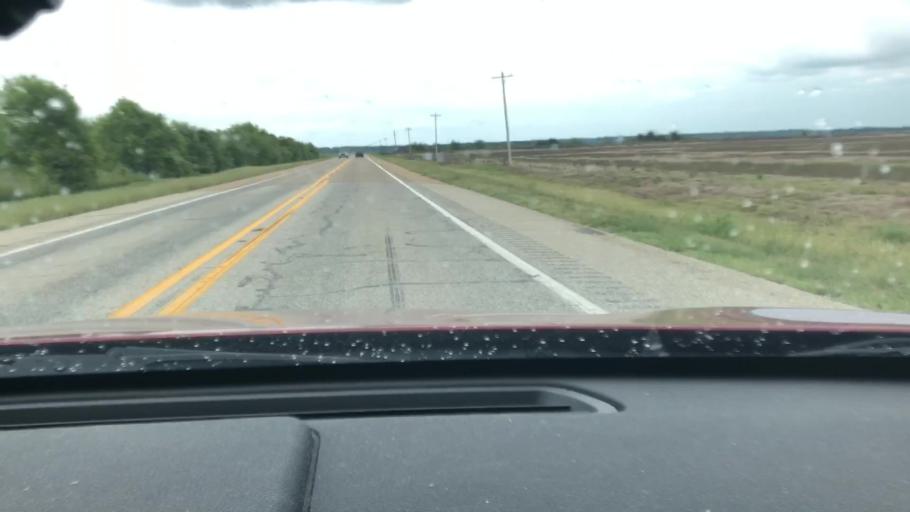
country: US
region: Arkansas
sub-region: Lafayette County
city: Lewisville
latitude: 33.4120
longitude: -93.7744
